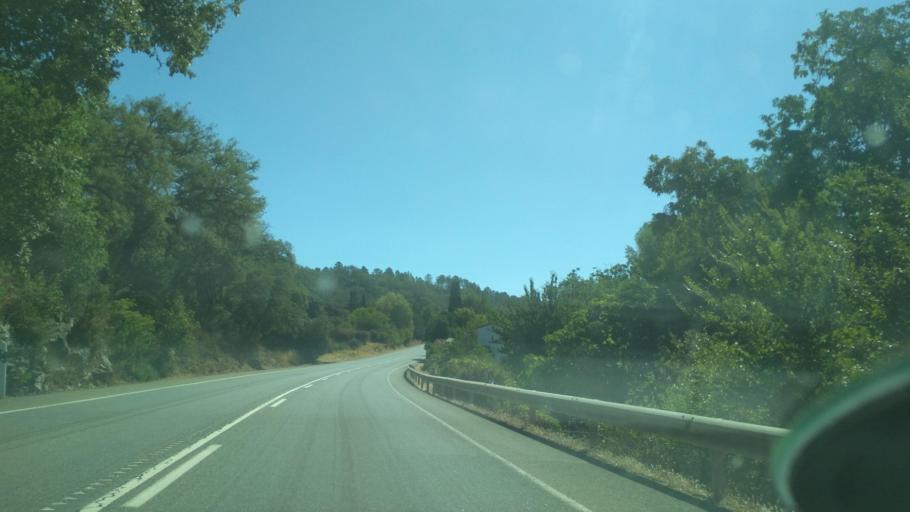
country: ES
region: Andalusia
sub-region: Provincia de Huelva
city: Fuenteheridos
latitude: 37.9165
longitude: -6.6768
